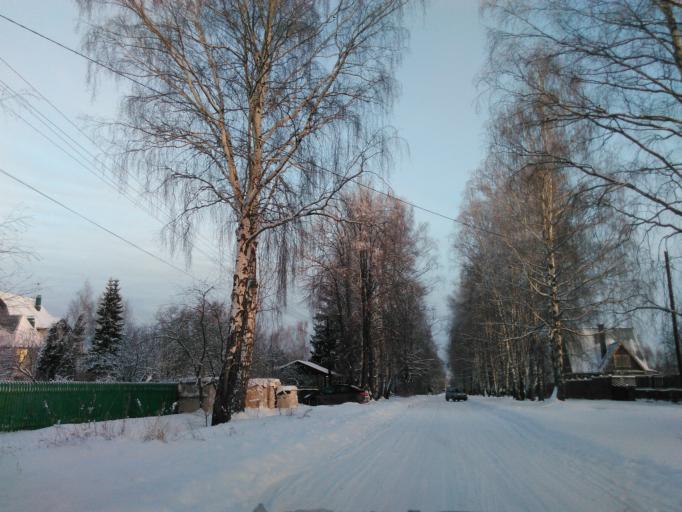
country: RU
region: Tverskaya
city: Zavidovo
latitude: 56.6392
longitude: 36.6283
